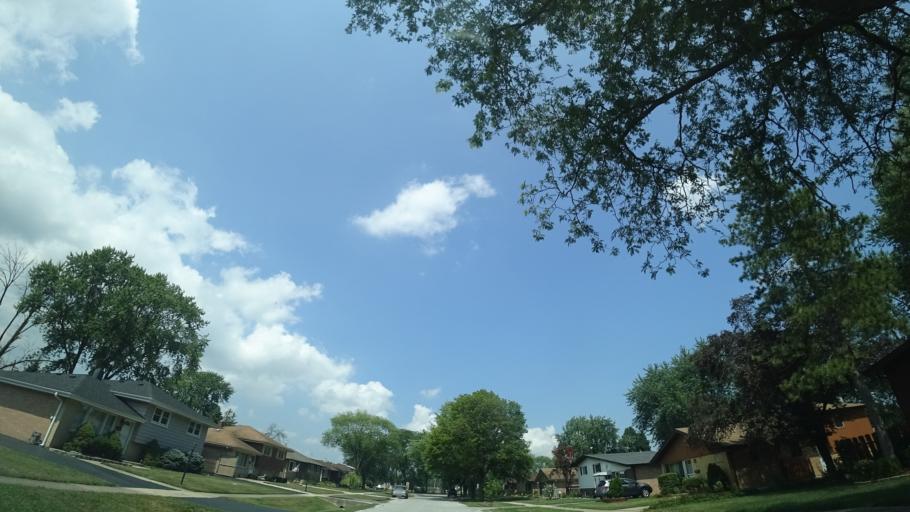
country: US
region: Illinois
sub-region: Cook County
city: Chicago Ridge
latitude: 41.6948
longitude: -87.7876
